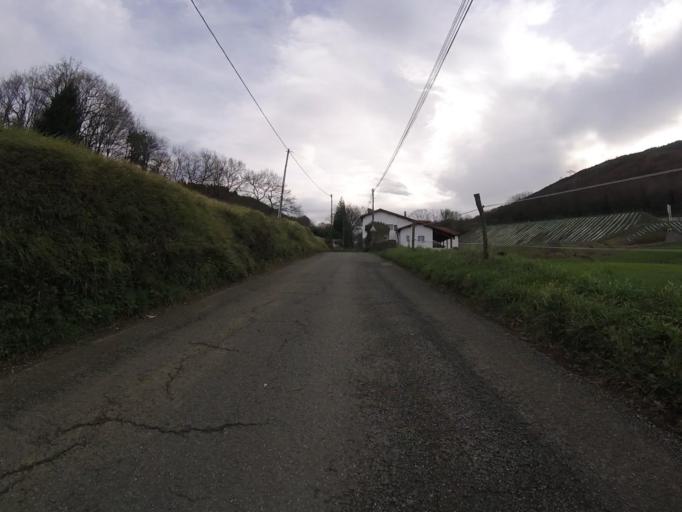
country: FR
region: Aquitaine
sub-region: Departement des Pyrenees-Atlantiques
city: Urrugne
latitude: 43.3423
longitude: -1.7373
